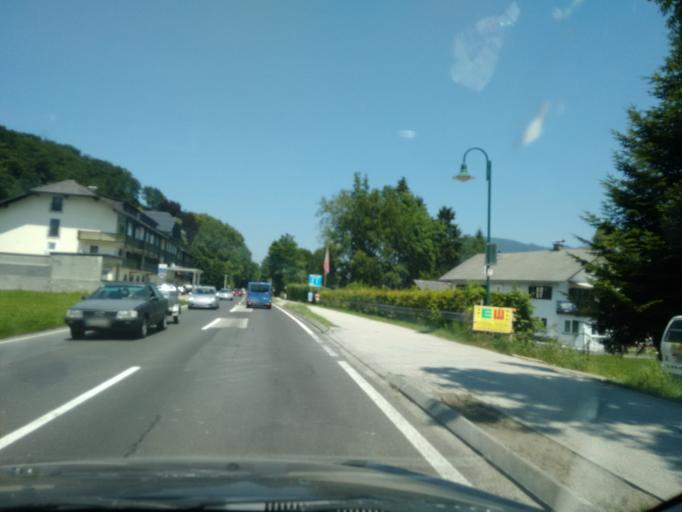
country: AT
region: Upper Austria
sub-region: Politischer Bezirk Gmunden
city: Altmunster
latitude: 47.8670
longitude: 13.7775
